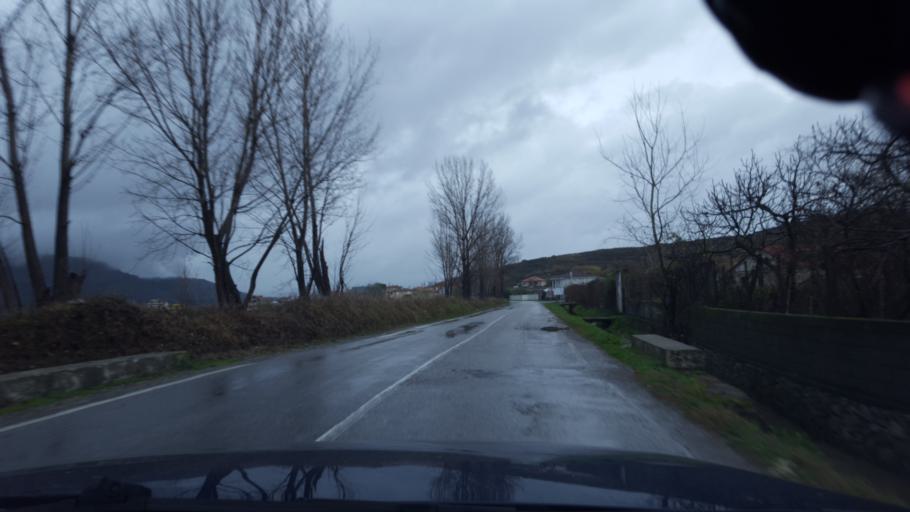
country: AL
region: Shkoder
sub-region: Rrethi i Shkodres
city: Berdica e Madhe
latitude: 42.0065
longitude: 19.4796
